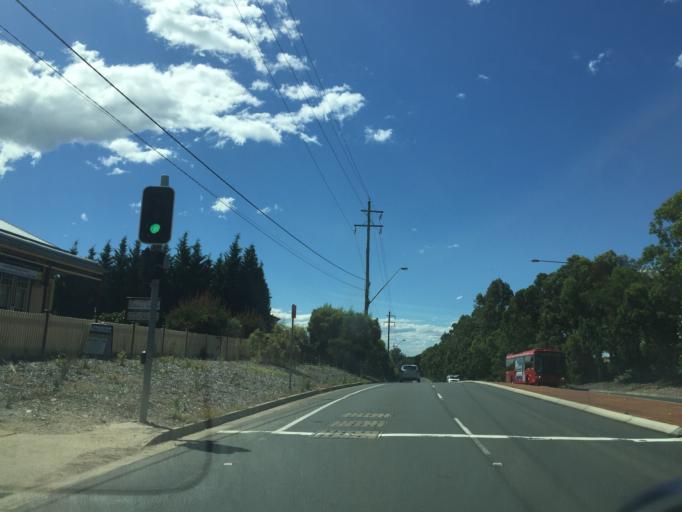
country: AU
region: New South Wales
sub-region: The Hills Shire
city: Glenhaven
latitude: -33.7061
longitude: 150.9726
